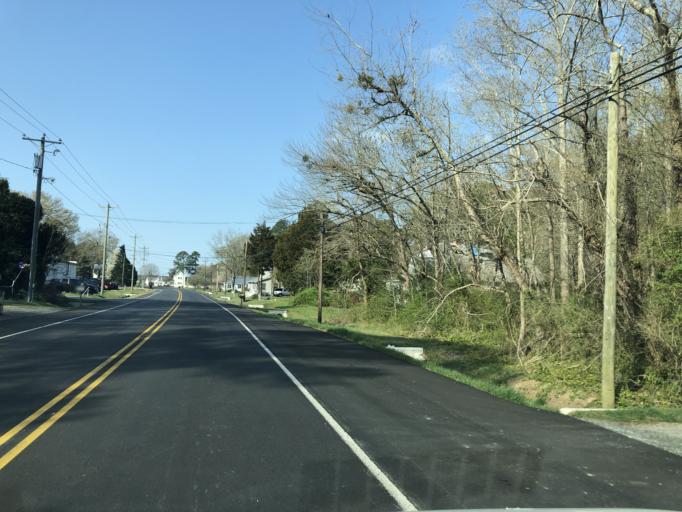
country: US
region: Maryland
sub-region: Dorchester County
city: Algonquin
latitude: 38.5102
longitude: -76.1441
